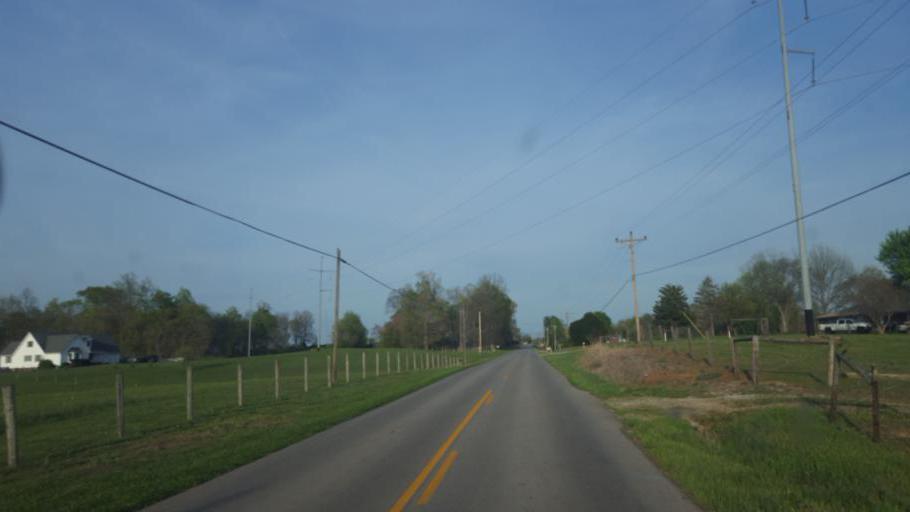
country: US
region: Kentucky
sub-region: Barren County
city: Glasgow
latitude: 36.9450
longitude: -85.9984
